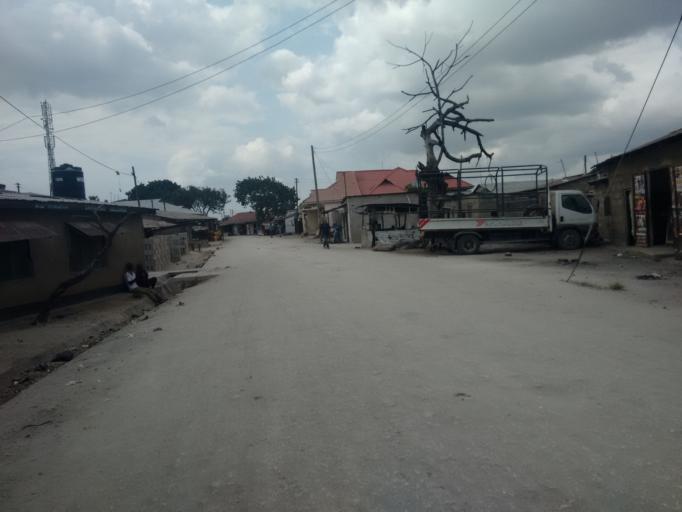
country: TZ
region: Dar es Salaam
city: Dar es Salaam
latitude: -6.8576
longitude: 39.2537
